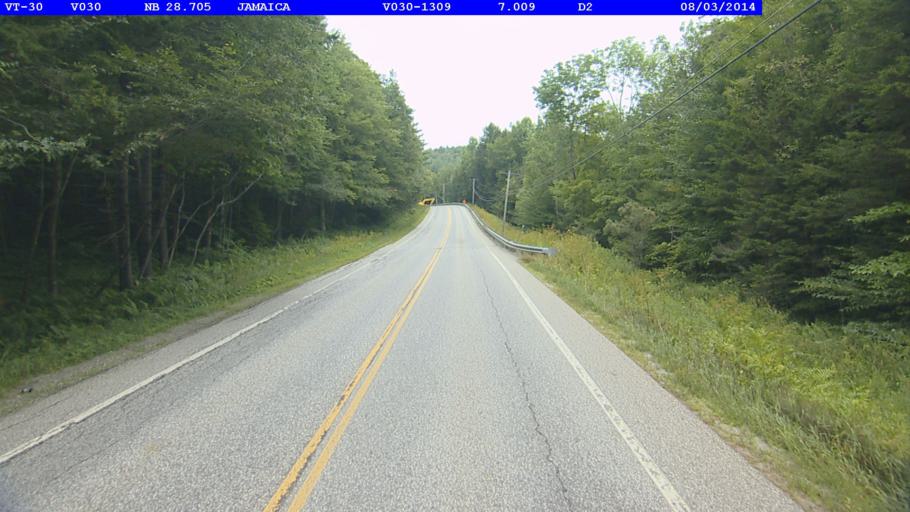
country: US
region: Vermont
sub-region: Windham County
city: Dover
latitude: 43.1310
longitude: -72.8144
